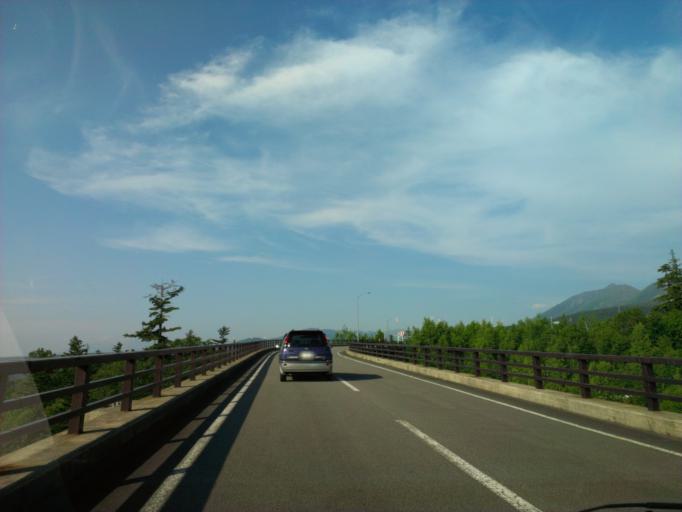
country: JP
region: Hokkaido
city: Shimo-furano
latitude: 43.4600
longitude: 142.6446
